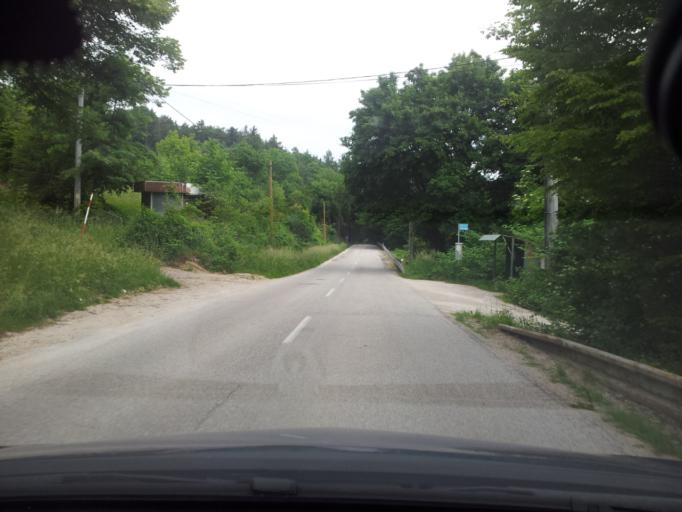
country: SK
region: Nitriansky
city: Partizanske
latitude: 48.5830
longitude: 18.4531
